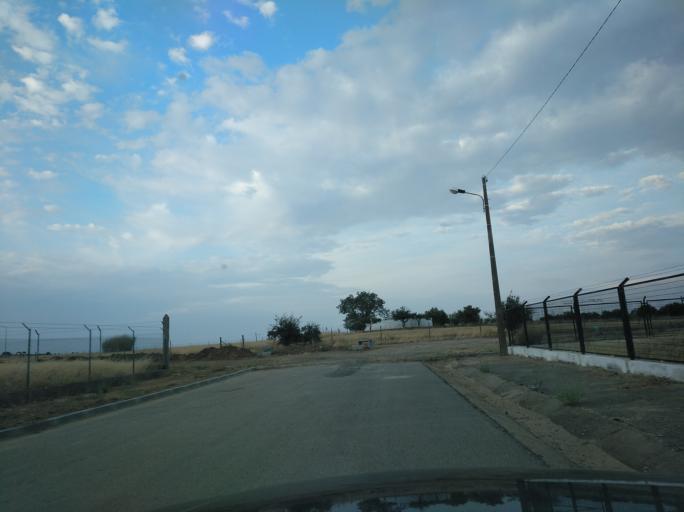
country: PT
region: Portalegre
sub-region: Campo Maior
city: Campo Maior
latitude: 39.0241
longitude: -7.0586
